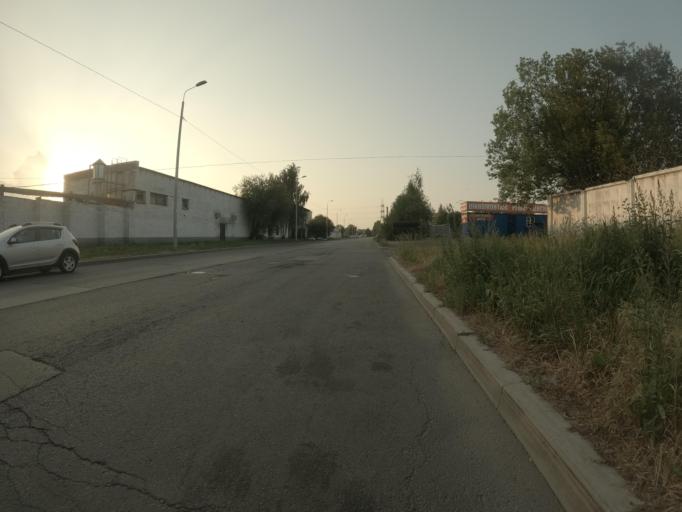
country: RU
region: St.-Petersburg
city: Krasnogvargeisky
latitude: 59.9717
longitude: 30.4409
